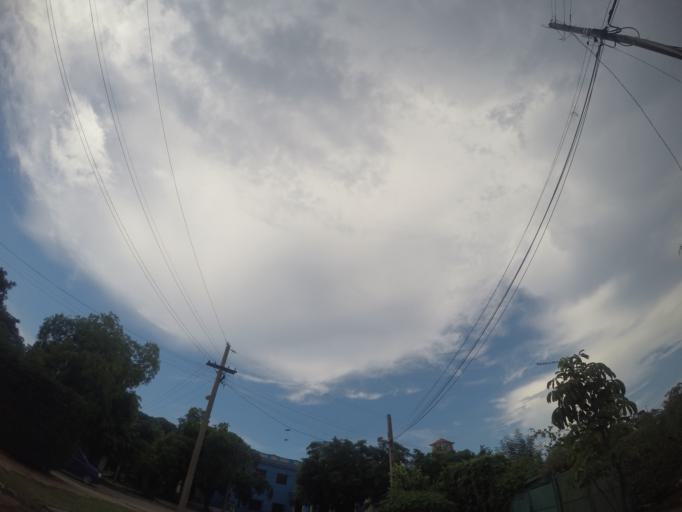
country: CU
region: La Habana
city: Havana
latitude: 23.1171
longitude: -82.4215
